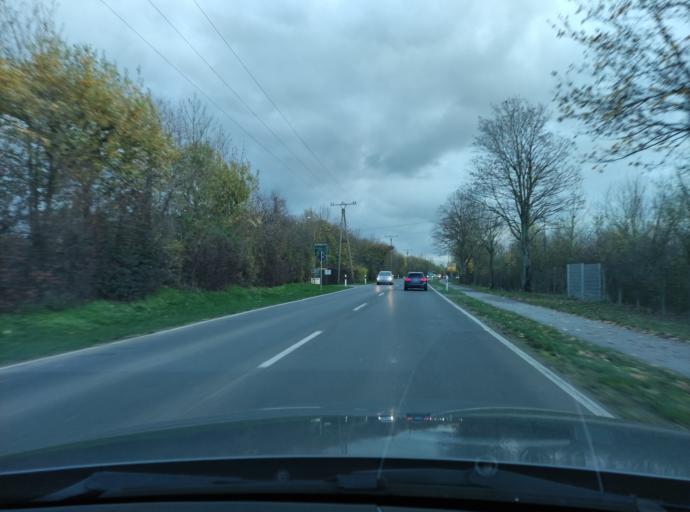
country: DE
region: North Rhine-Westphalia
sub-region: Regierungsbezirk Dusseldorf
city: Dormagen
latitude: 51.1035
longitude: 6.7933
